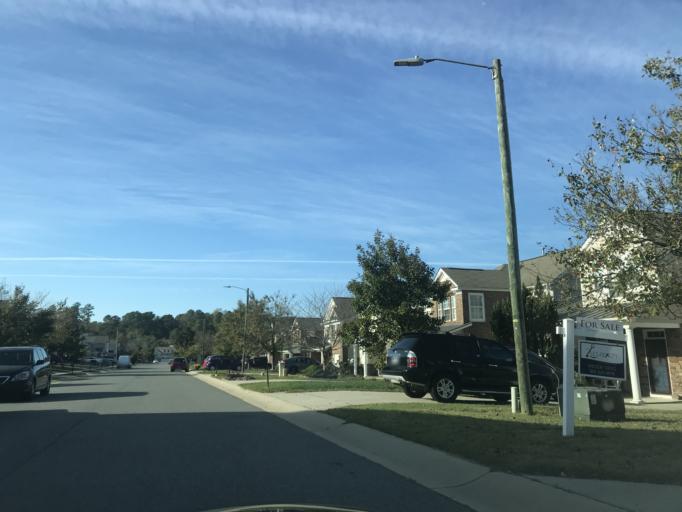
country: US
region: North Carolina
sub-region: Wake County
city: Wake Forest
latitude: 35.9003
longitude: -78.5484
